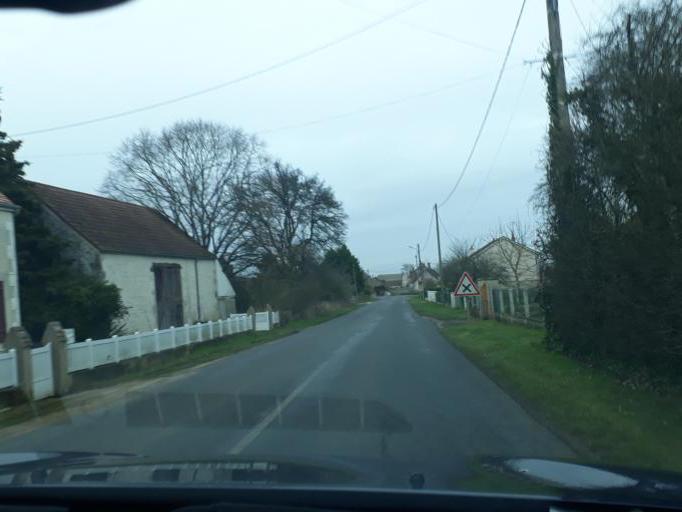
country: FR
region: Centre
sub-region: Departement du Loir-et-Cher
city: Ouzouer-le-Marche
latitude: 47.8492
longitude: 1.4454
